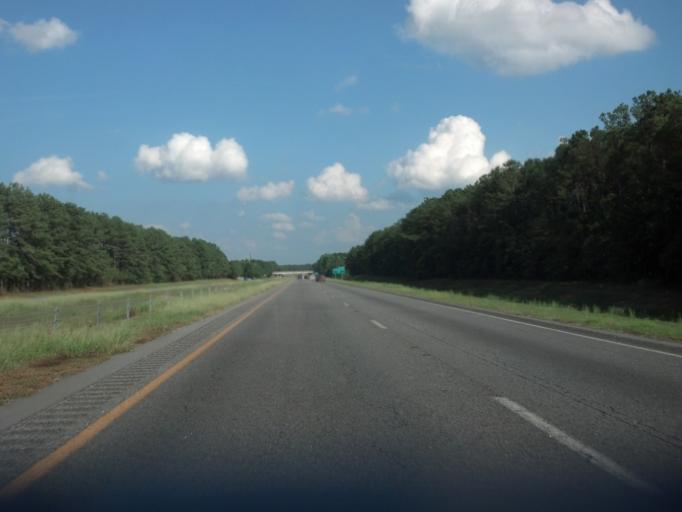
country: US
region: North Carolina
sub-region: Nash County
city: Rocky Mount
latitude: 35.9278
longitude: -77.6860
